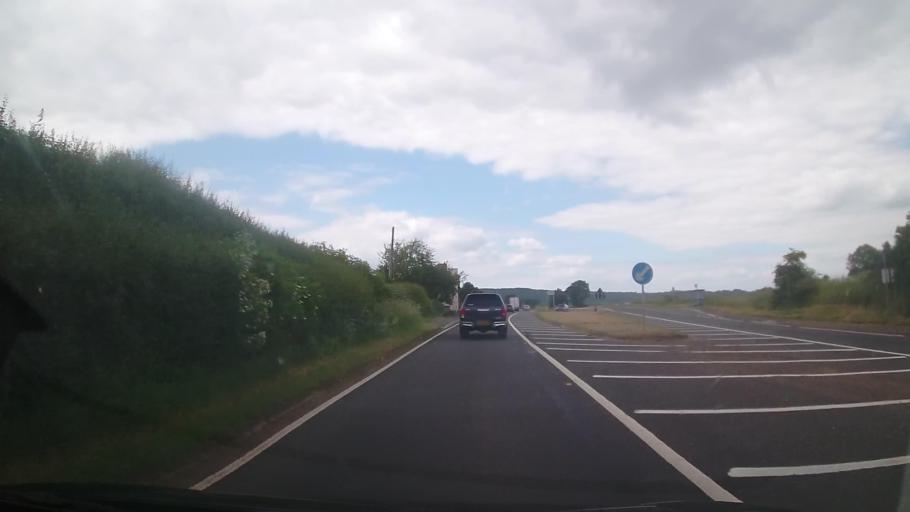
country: GB
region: England
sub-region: Herefordshire
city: Wellington
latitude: 52.1282
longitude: -2.7315
